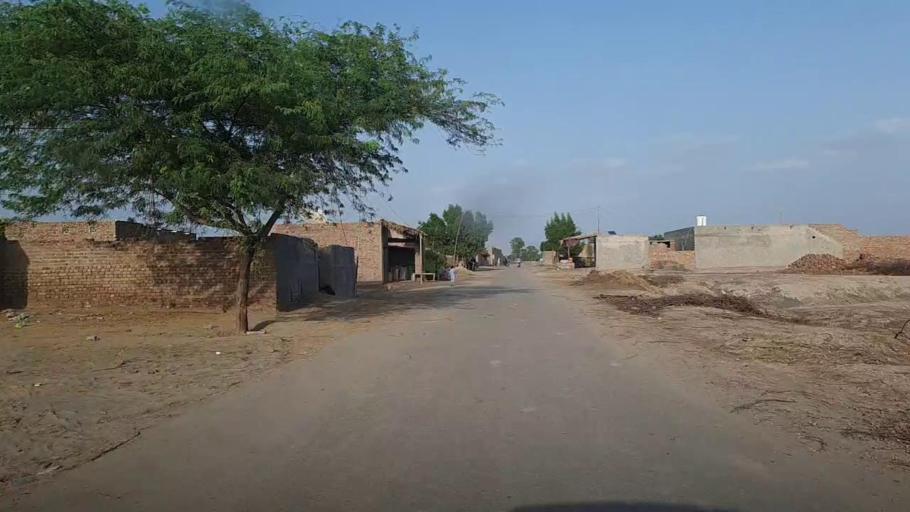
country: PK
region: Sindh
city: Khairpur
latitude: 28.0829
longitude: 69.7907
